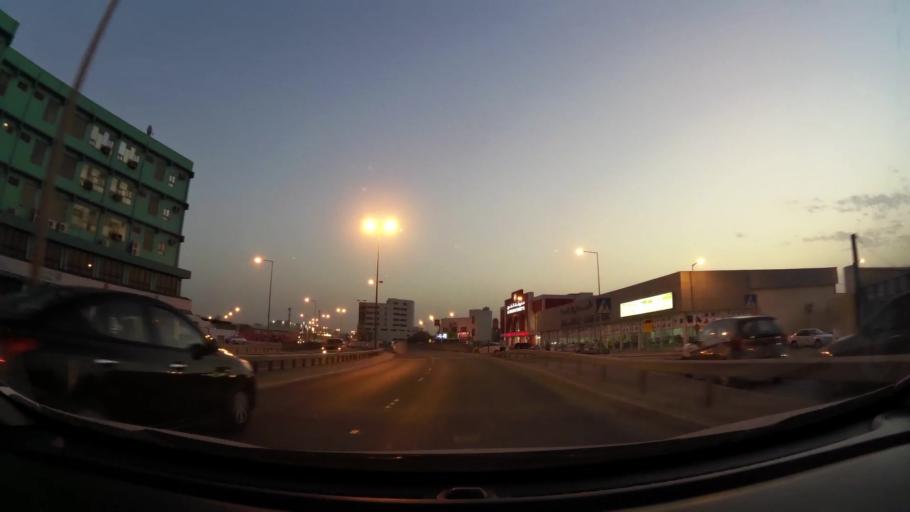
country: BH
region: Manama
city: Jidd Hafs
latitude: 26.2118
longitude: 50.5554
